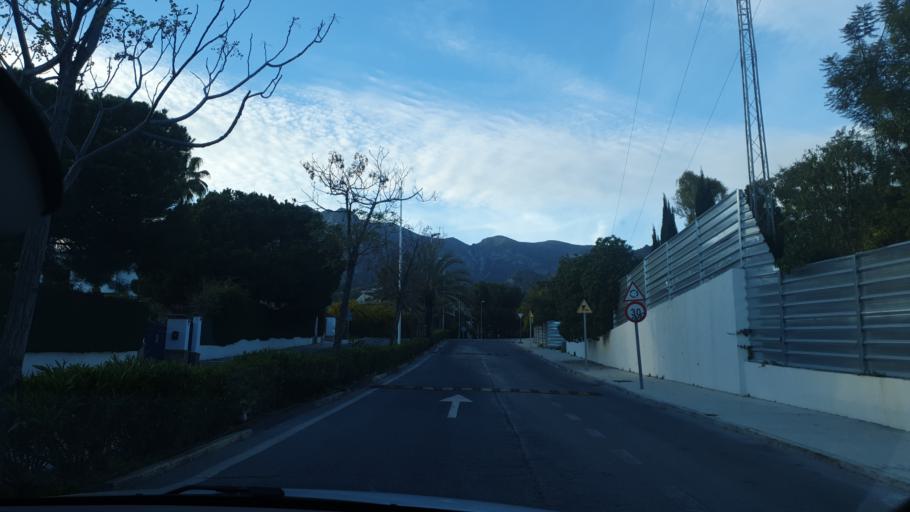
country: ES
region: Andalusia
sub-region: Provincia de Malaga
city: Marbella
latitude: 36.5246
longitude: -4.8929
